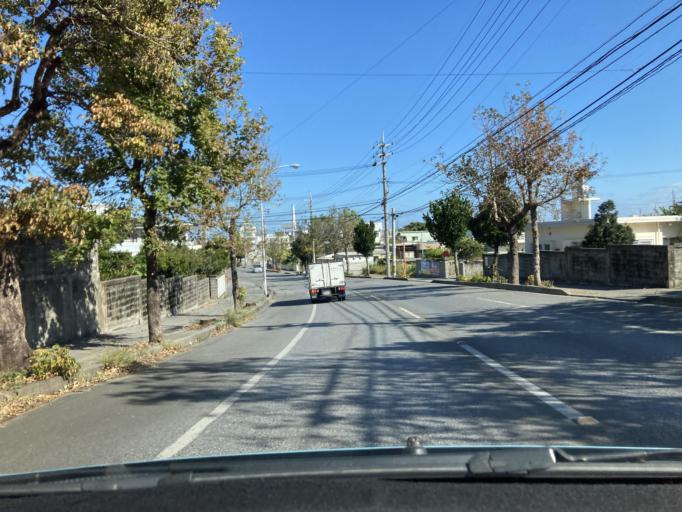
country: JP
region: Okinawa
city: Gushikawa
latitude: 26.3670
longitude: 127.8579
